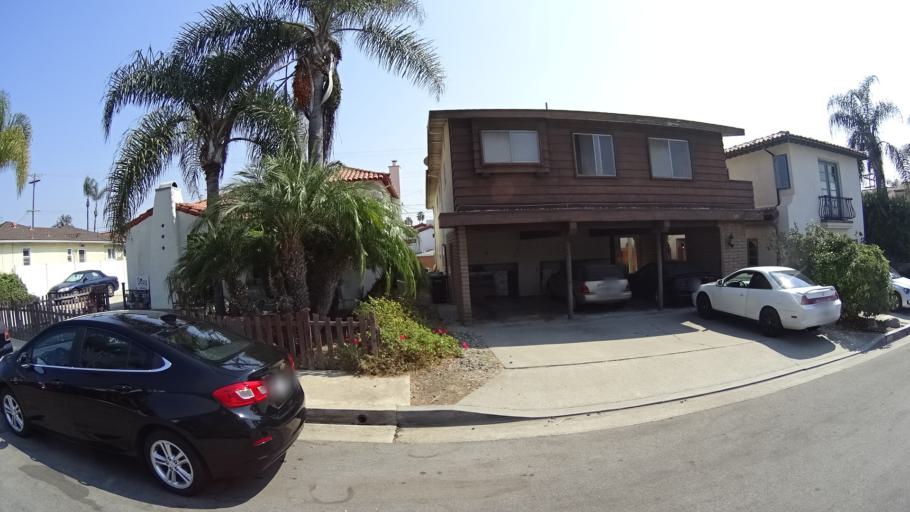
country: US
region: California
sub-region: Orange County
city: San Clemente
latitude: 33.4234
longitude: -117.6193
